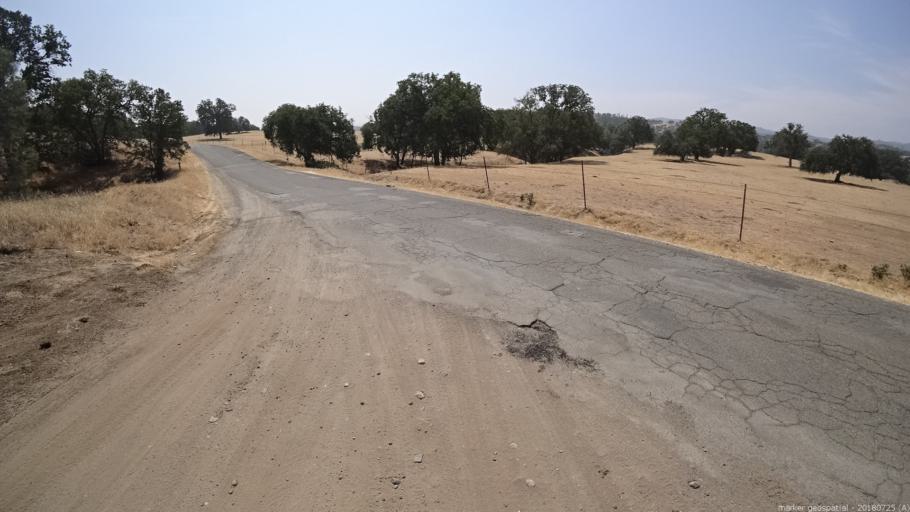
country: US
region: California
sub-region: San Luis Obispo County
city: Shandon
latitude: 35.8766
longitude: -120.4165
